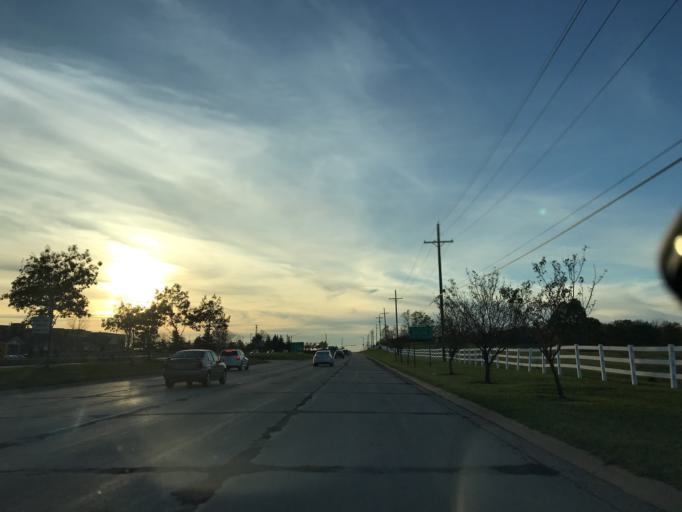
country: US
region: Michigan
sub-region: Oakland County
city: Novi
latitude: 42.4963
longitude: -83.4576
